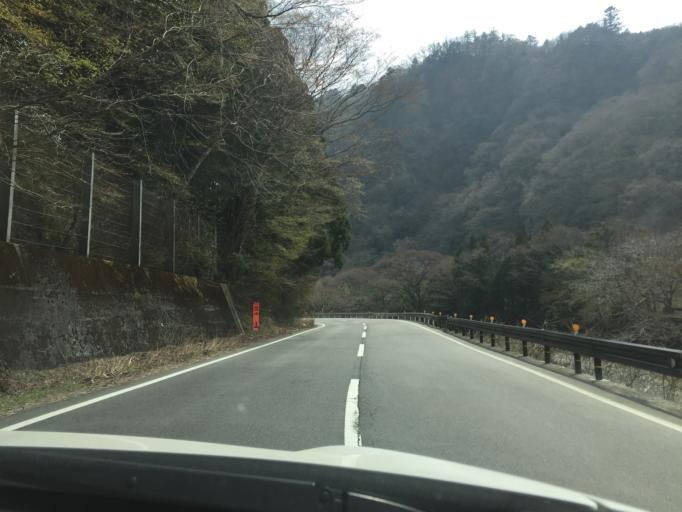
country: JP
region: Fukushima
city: Iwaki
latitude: 37.0226
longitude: 140.6632
